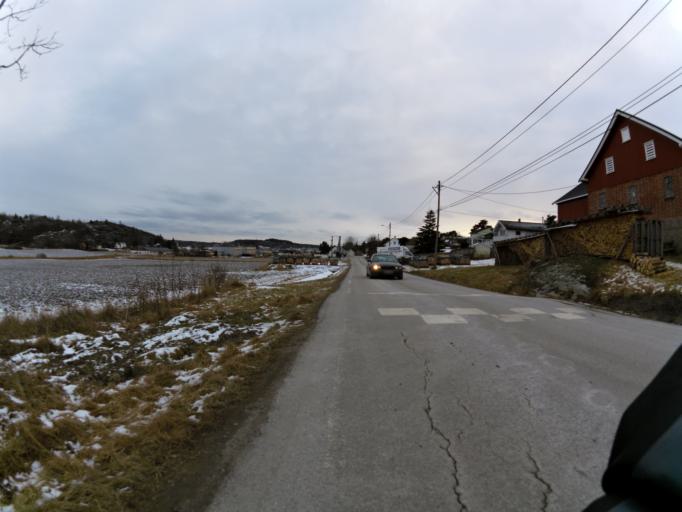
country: NO
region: Ostfold
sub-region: Fredrikstad
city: Fredrikstad
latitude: 59.2154
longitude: 10.8907
